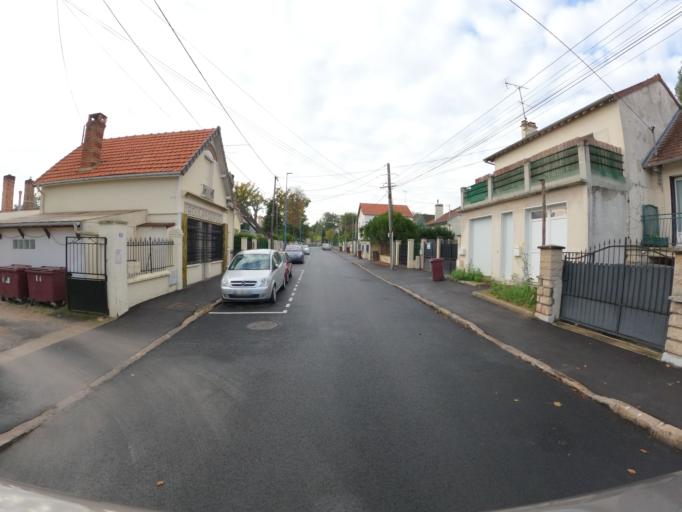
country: FR
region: Ile-de-France
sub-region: Departement de Seine-Saint-Denis
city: Montfermeil
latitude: 48.9000
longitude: 2.5908
